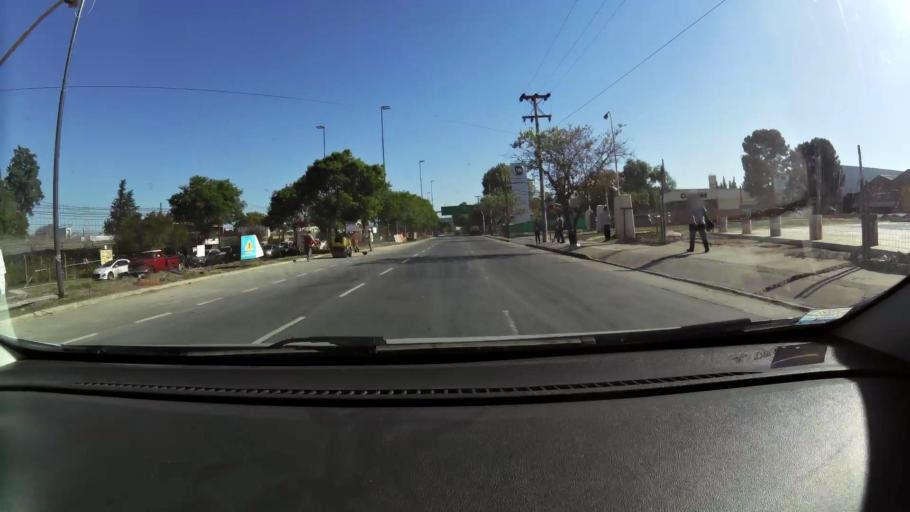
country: AR
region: Cordoba
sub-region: Departamento de Capital
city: Cordoba
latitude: -31.3578
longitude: -64.2035
